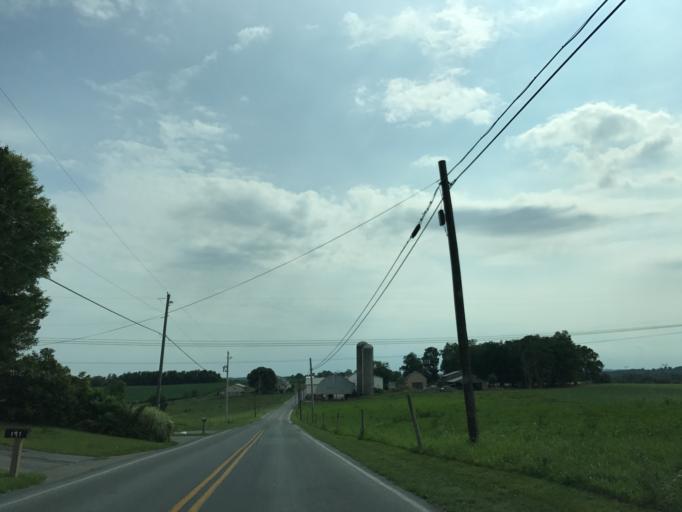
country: US
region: Pennsylvania
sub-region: Lancaster County
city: Quarryville
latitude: 39.7720
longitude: -76.1992
